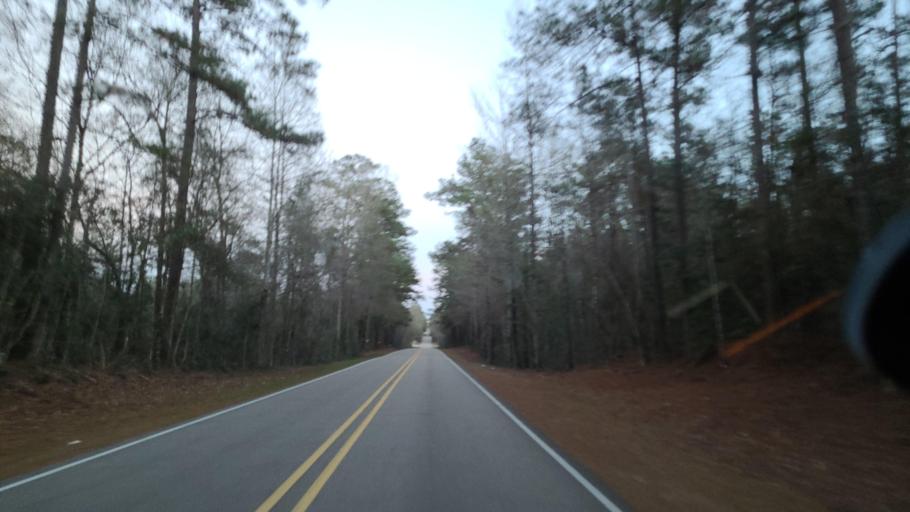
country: US
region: Mississippi
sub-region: Forrest County
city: Hattiesburg
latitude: 31.2120
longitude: -89.2582
